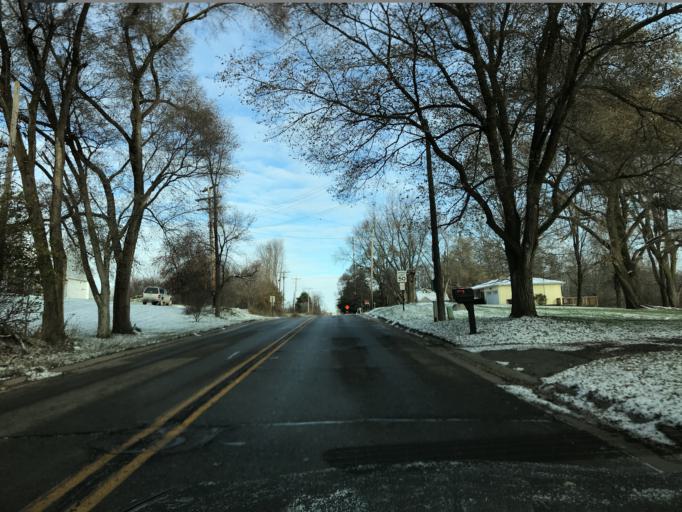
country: US
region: Michigan
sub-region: Eaton County
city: Dimondale
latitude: 42.6745
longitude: -84.6423
